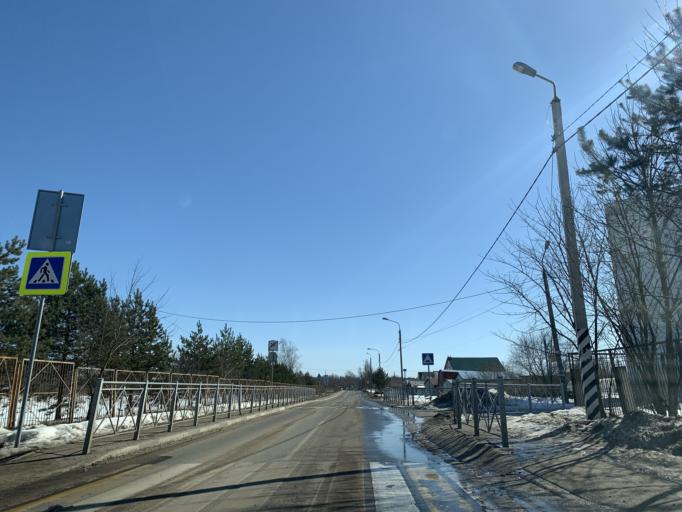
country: RU
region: Jaroslavl
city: Konstantinovskiy
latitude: 57.8392
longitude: 39.5820
